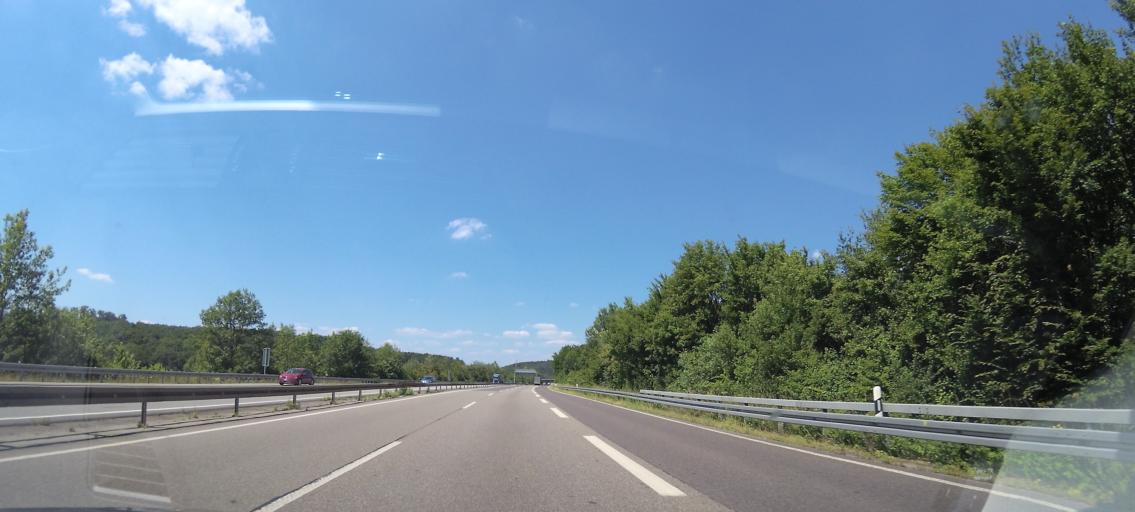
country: DE
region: Saarland
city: Friedrichsthal
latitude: 49.3245
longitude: 7.0759
